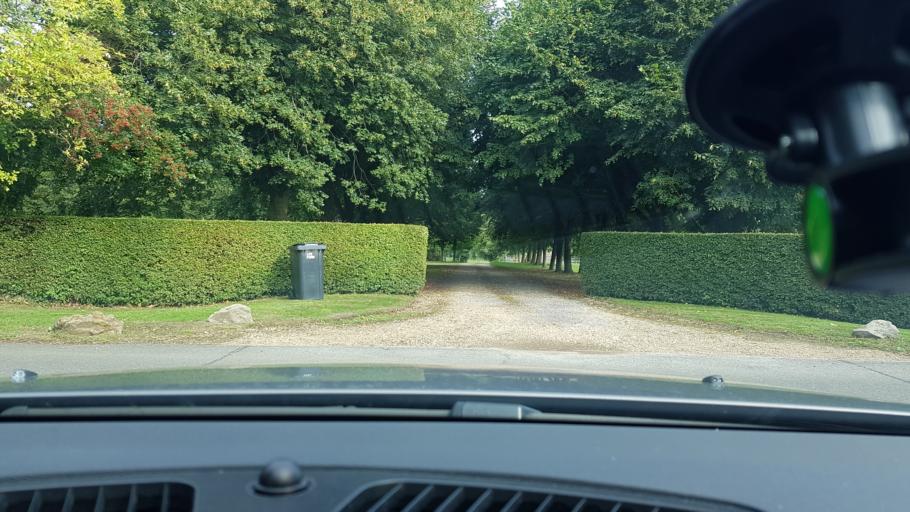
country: GB
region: England
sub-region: Wiltshire
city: Chilton Foliat
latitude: 51.4689
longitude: -1.5410
